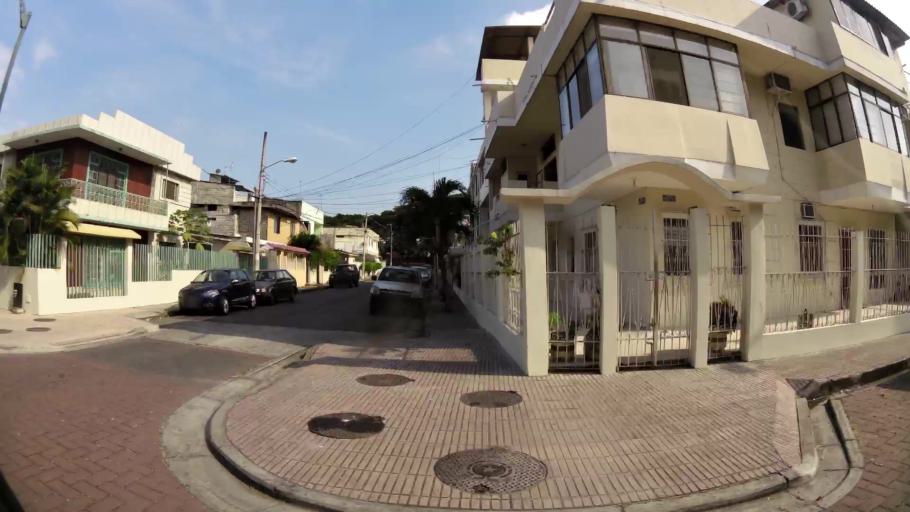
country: EC
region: Guayas
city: Guayaquil
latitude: -2.1874
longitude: -79.9009
